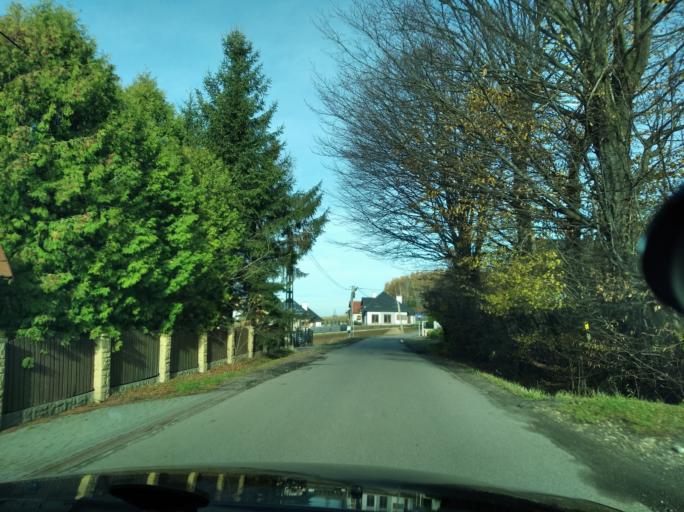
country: PL
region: Subcarpathian Voivodeship
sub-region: Powiat rzeszowski
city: Tyczyn
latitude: 49.9962
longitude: 22.0668
